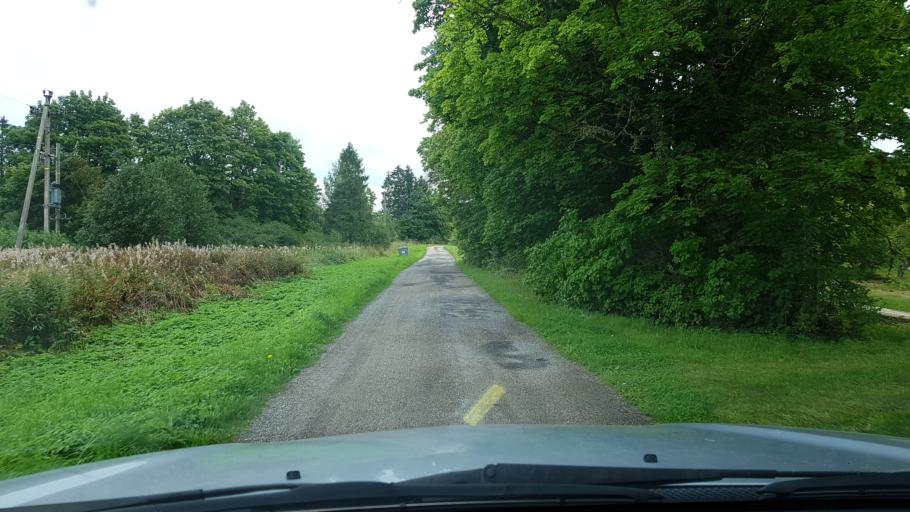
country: EE
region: Harju
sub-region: Joelaehtme vald
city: Loo
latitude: 59.4119
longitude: 24.9612
